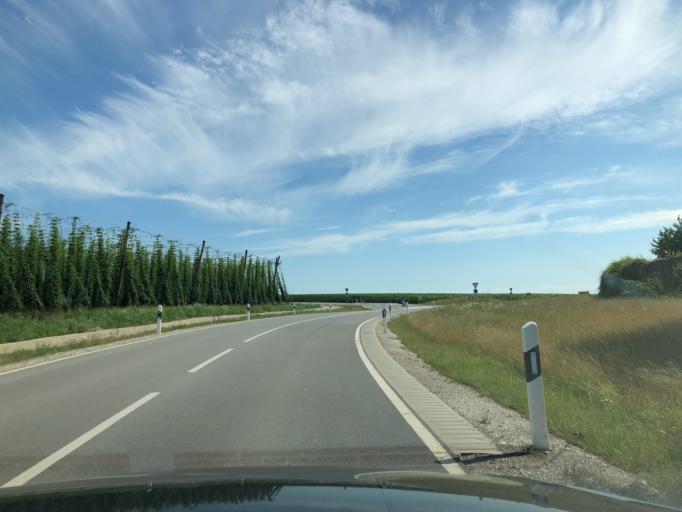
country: DE
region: Bavaria
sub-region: Regierungsbezirk Mittelfranken
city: Greding
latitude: 49.0443
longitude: 11.4107
